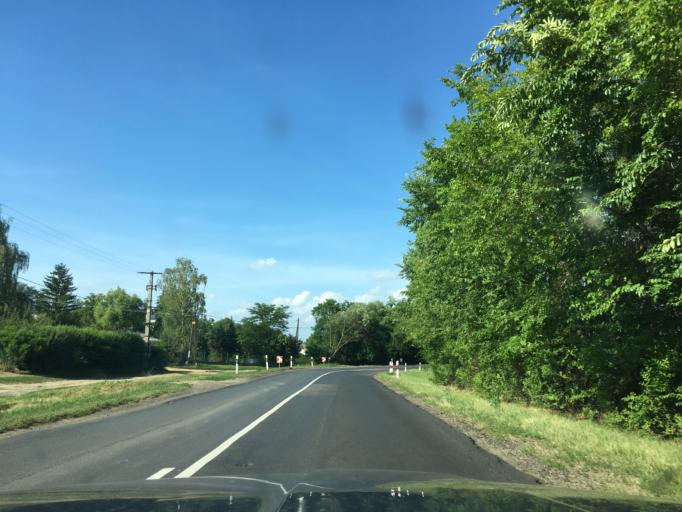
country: HU
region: Hajdu-Bihar
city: Hajdusamson
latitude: 47.5829
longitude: 21.7160
